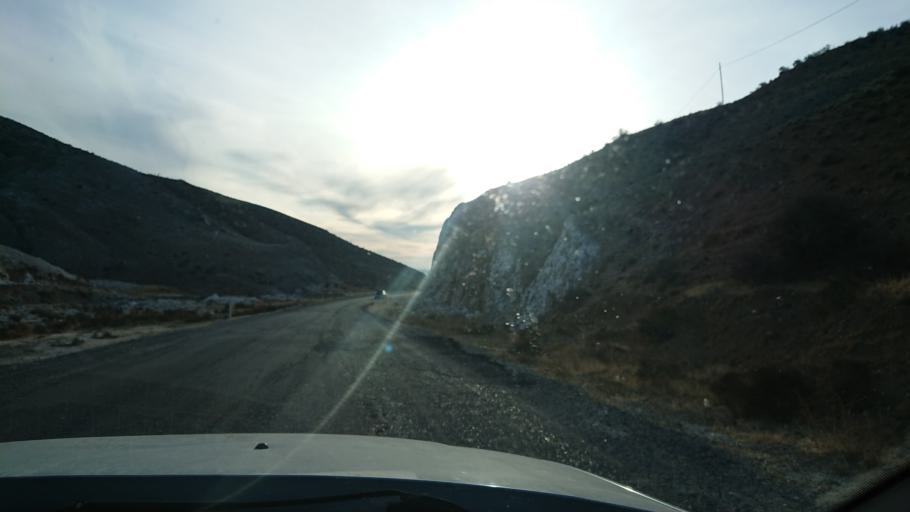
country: TR
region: Ankara
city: Sereflikochisar
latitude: 38.7506
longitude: 33.6897
